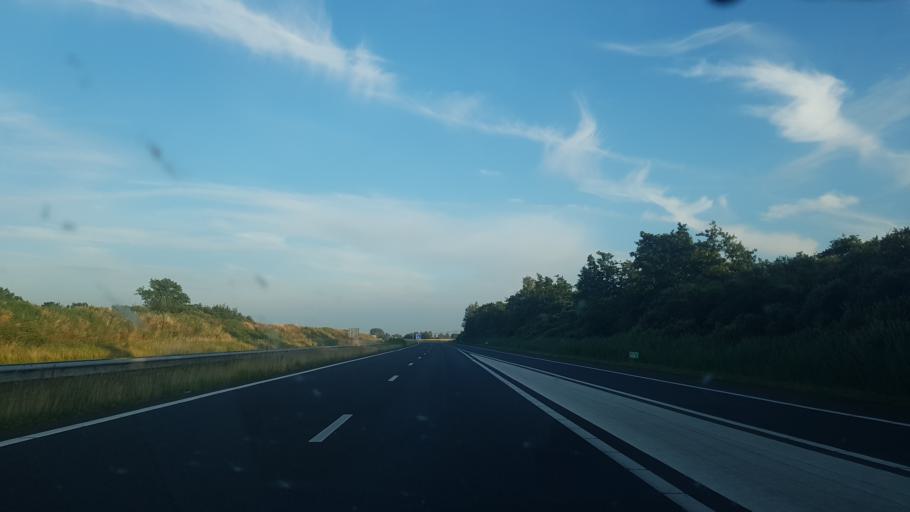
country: NL
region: Friesland
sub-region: Gemeente Boarnsterhim
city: Grou
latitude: 53.1072
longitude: 5.8150
